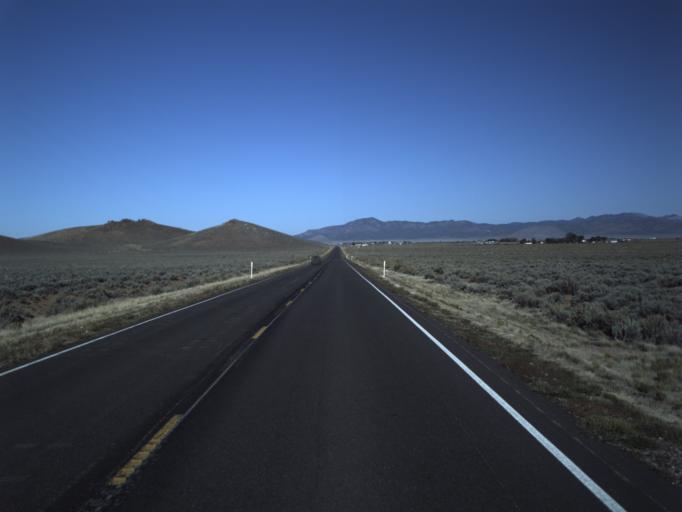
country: US
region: Utah
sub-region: Washington County
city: Enterprise
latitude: 37.7371
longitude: -113.7332
